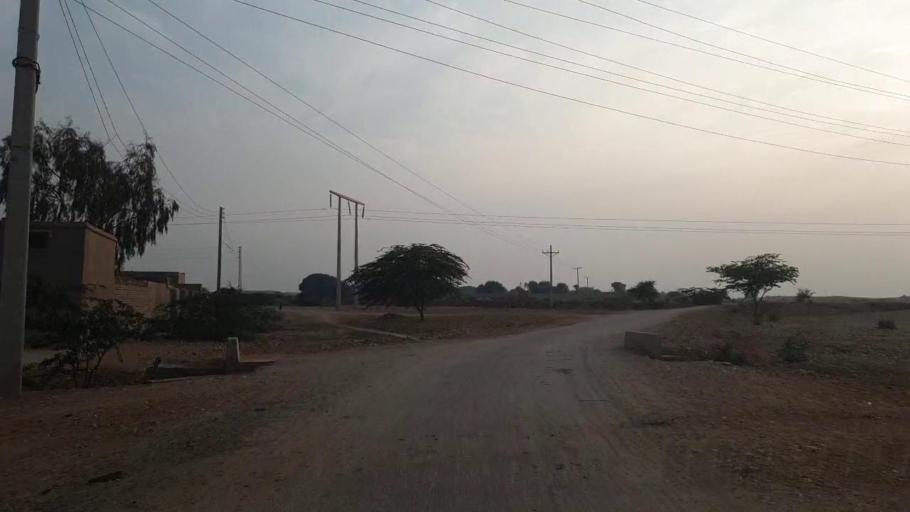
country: PK
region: Sindh
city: Sann
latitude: 26.1631
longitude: 68.0075
